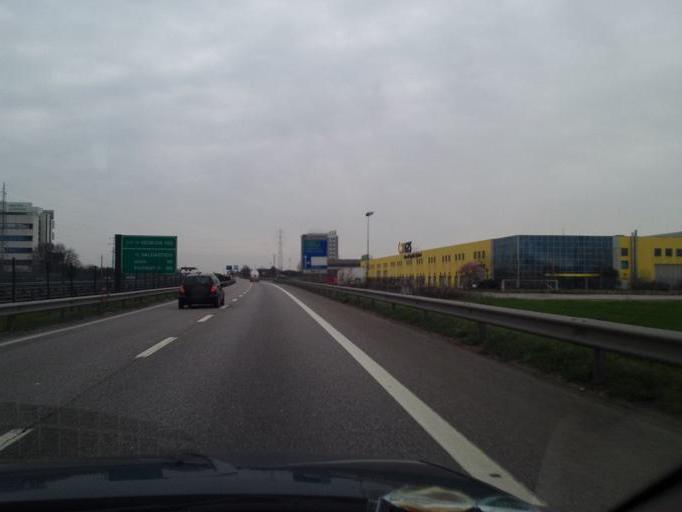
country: IT
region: Veneto
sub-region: Provincia di Verona
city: Beccacivetta-Azzano
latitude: 45.3968
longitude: 10.9826
